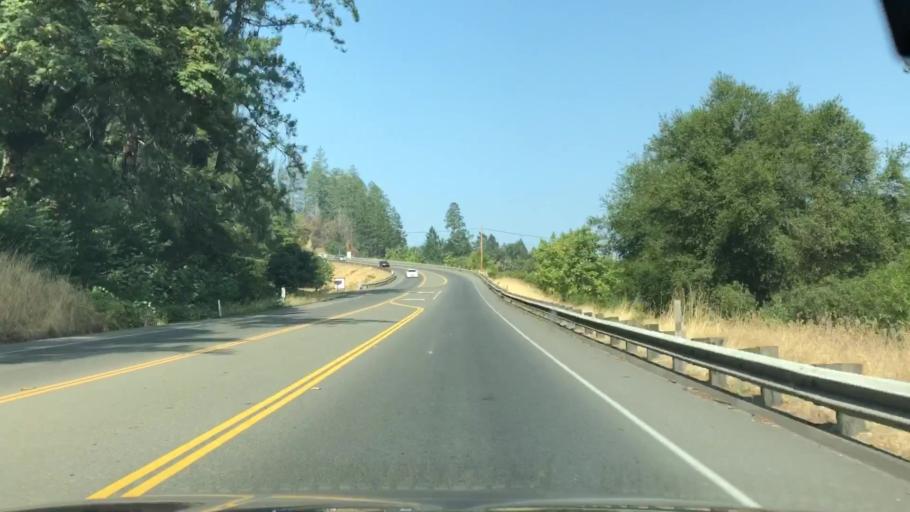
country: US
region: California
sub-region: Napa County
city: Calistoga
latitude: 38.5779
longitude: -122.6151
